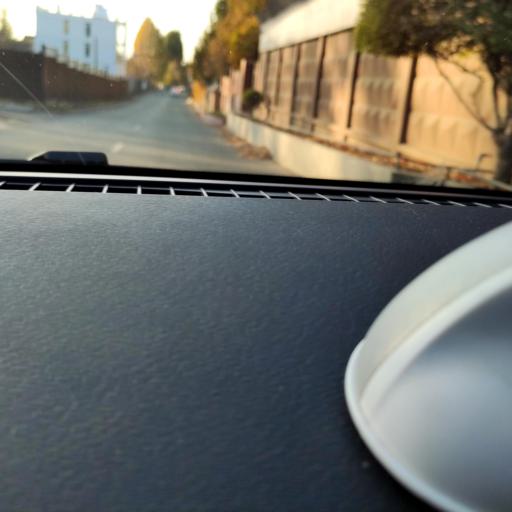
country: RU
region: Samara
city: Samara
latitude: 53.2269
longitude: 50.1693
